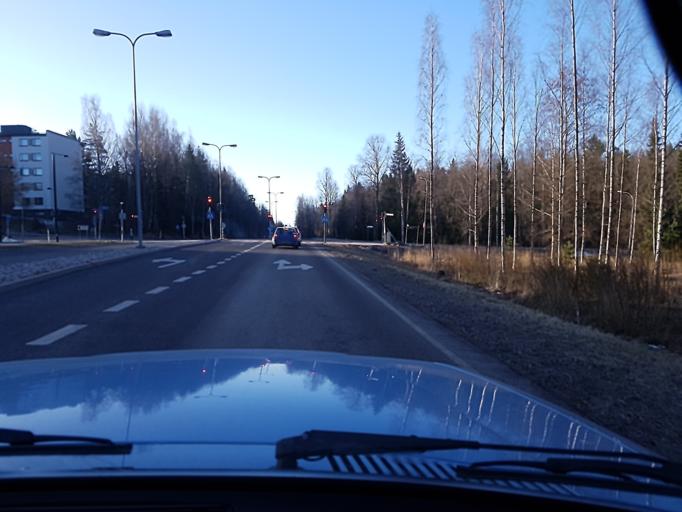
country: FI
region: Uusimaa
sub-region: Helsinki
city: Kilo
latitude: 60.2703
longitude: 24.8408
